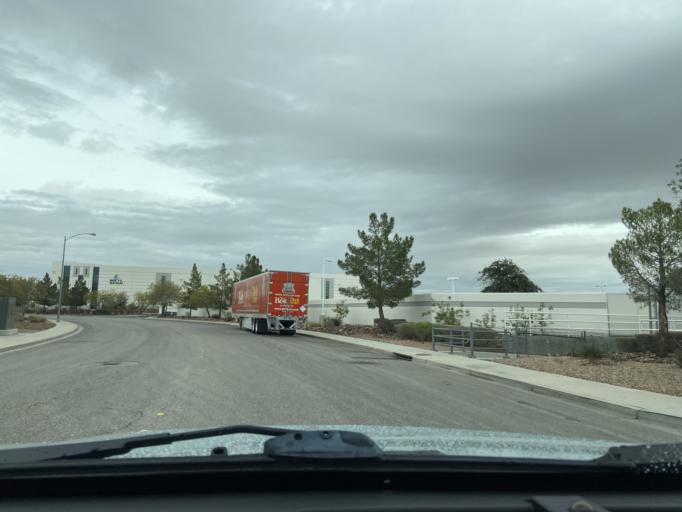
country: US
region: Nevada
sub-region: Clark County
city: Sunrise Manor
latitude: 36.2436
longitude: -115.1051
